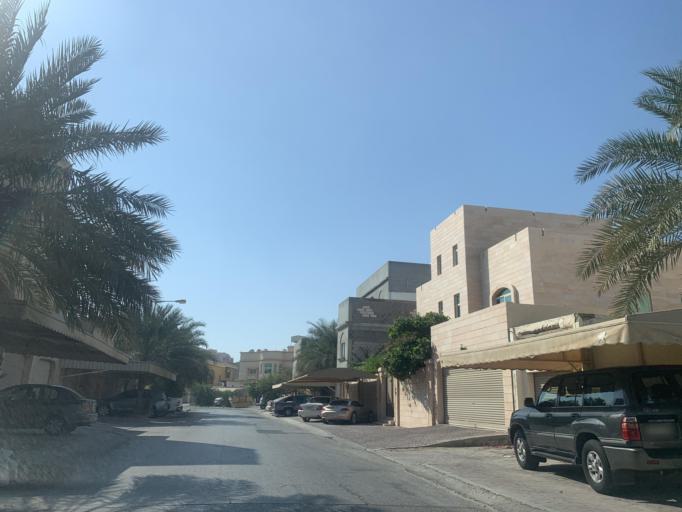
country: BH
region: Central Governorate
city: Madinat Hamad
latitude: 26.1235
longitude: 50.4922
